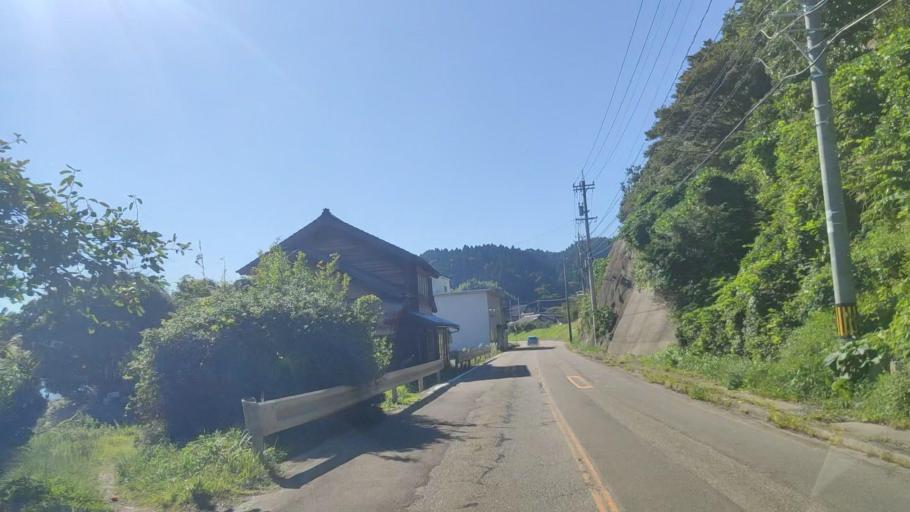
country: JP
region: Ishikawa
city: Nanao
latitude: 37.2888
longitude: 137.1197
